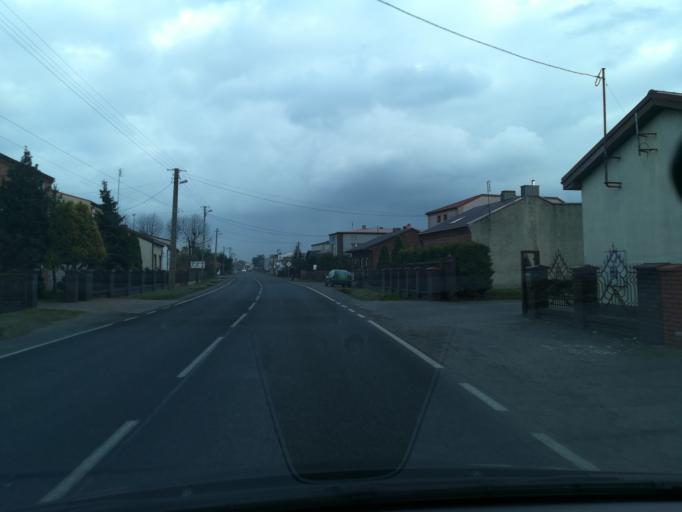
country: PL
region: Lodz Voivodeship
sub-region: Powiat radomszczanski
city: Radomsko
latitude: 51.0780
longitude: 19.3884
